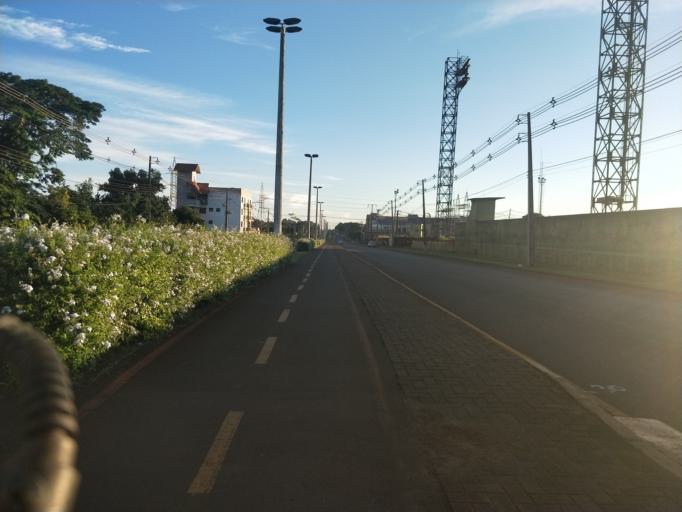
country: BR
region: Parana
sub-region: Marechal Candido Rondon
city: Marechal Candido Rondon
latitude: -24.5537
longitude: -54.0468
